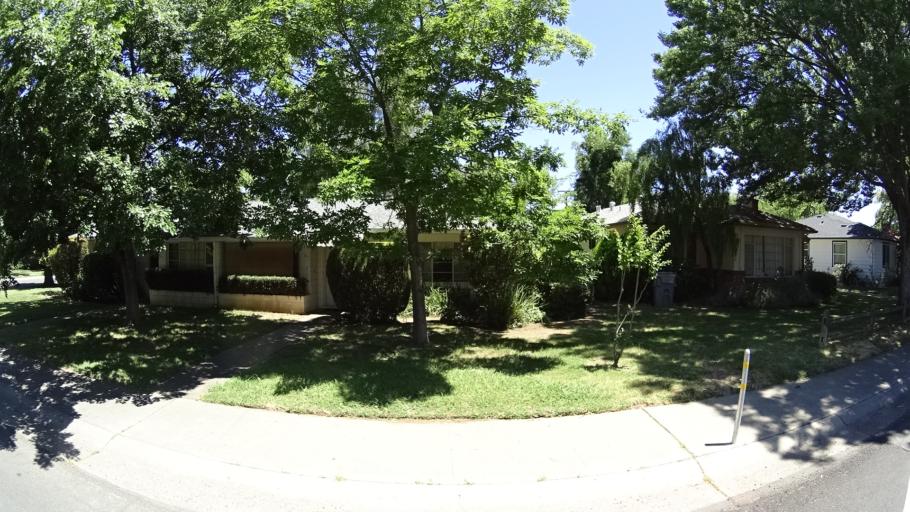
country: US
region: California
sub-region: Sacramento County
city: Sacramento
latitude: 38.5790
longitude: -121.4479
